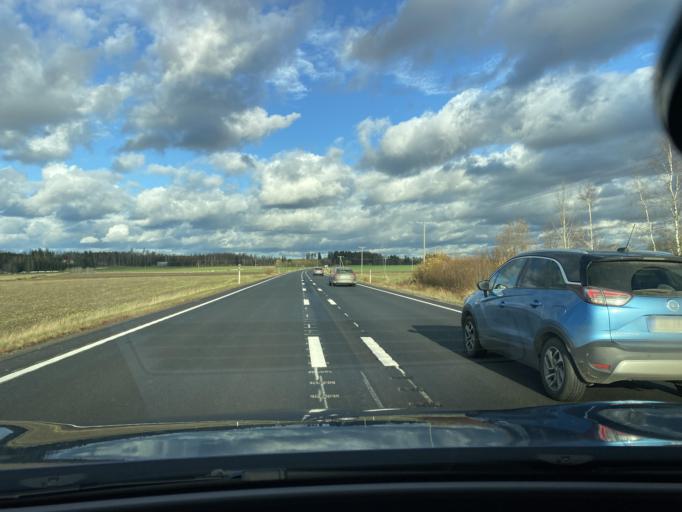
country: FI
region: Haeme
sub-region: Riihimaeki
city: Oitti
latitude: 60.8291
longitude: 25.0792
